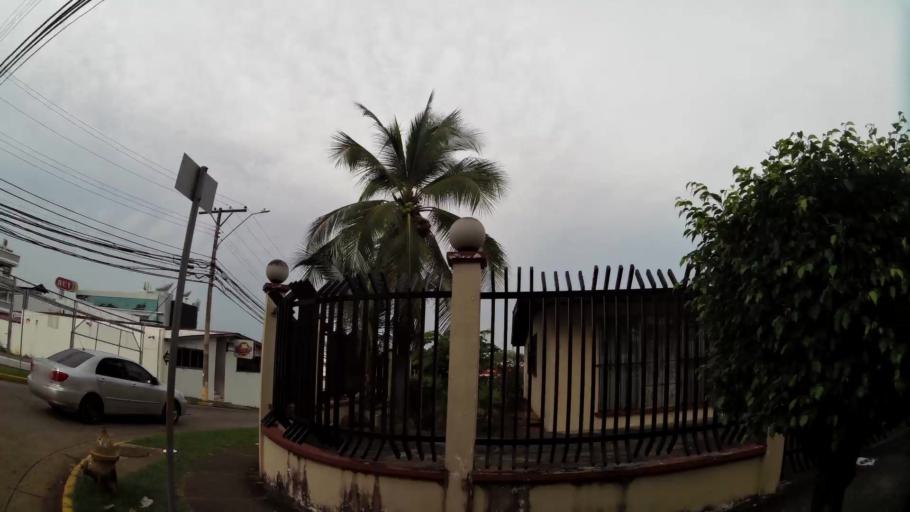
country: PA
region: Panama
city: Panama
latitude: 9.0100
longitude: -79.5099
